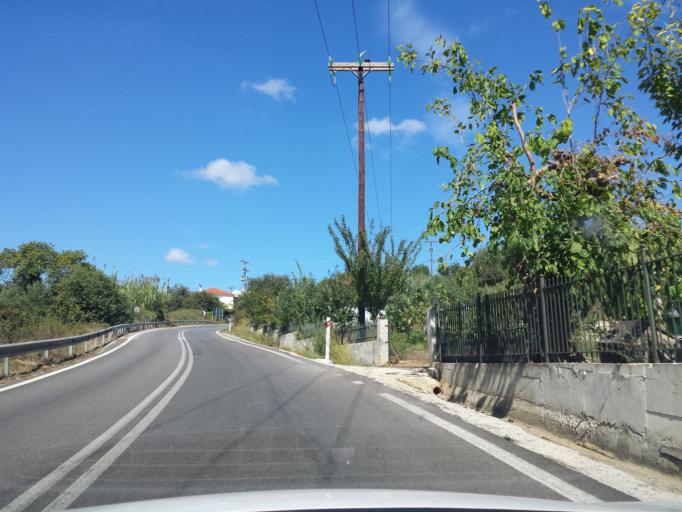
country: GR
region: Peloponnese
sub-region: Nomos Messinias
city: Pylos
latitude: 36.9500
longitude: 21.7598
